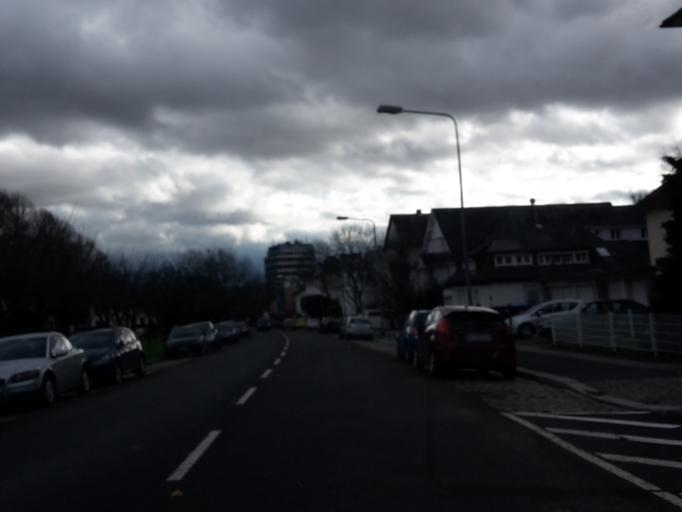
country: DE
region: Hesse
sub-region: Regierungsbezirk Darmstadt
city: Wiesbaden
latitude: 50.0890
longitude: 8.2204
